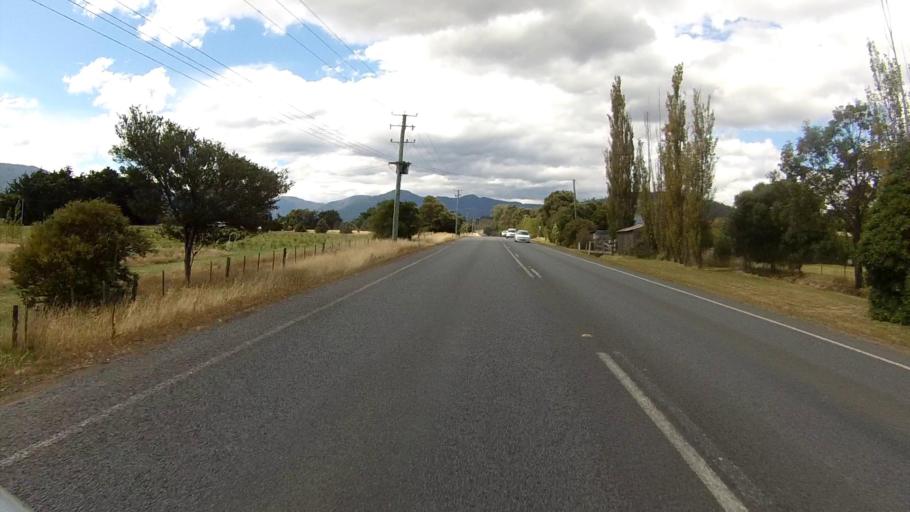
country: AU
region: Tasmania
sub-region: Huon Valley
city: Huonville
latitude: -42.9871
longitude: 147.0876
